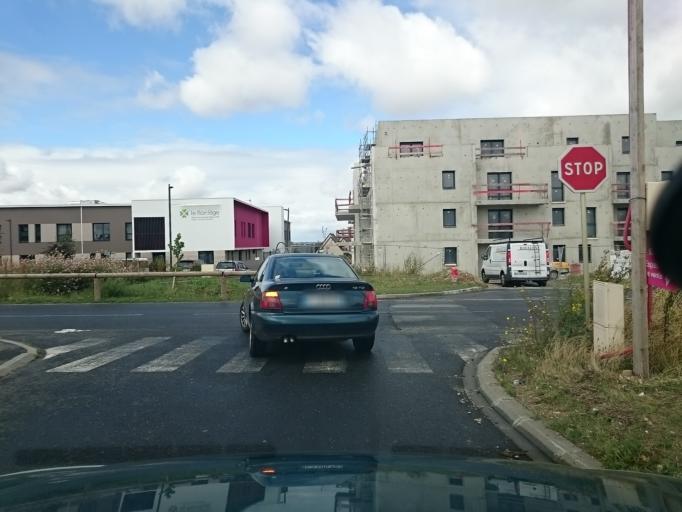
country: FR
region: Lower Normandy
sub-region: Departement du Calvados
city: Fleury-sur-Orne
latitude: 49.1409
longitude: -0.3767
